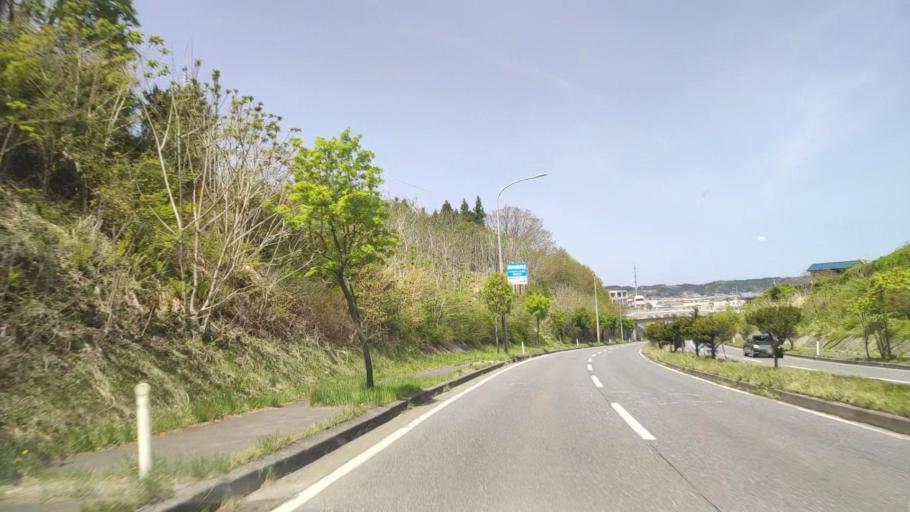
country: JP
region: Aomori
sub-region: Hachinohe Shi
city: Uchimaru
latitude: 40.4971
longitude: 141.4579
